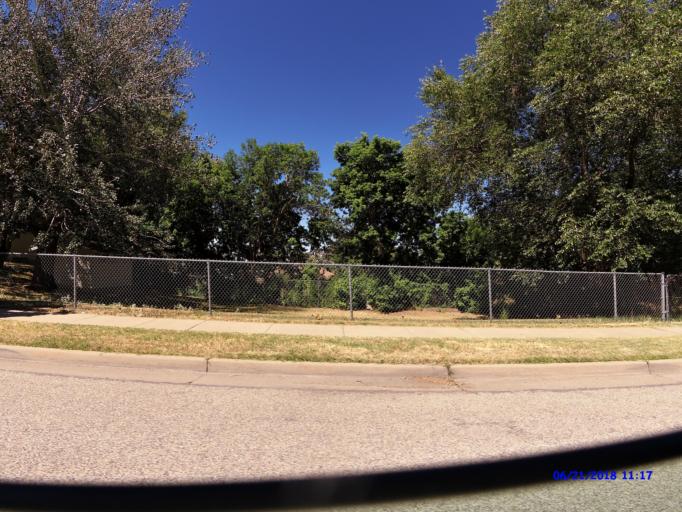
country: US
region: Utah
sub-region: Weber County
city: Ogden
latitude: 41.2576
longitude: -111.9557
